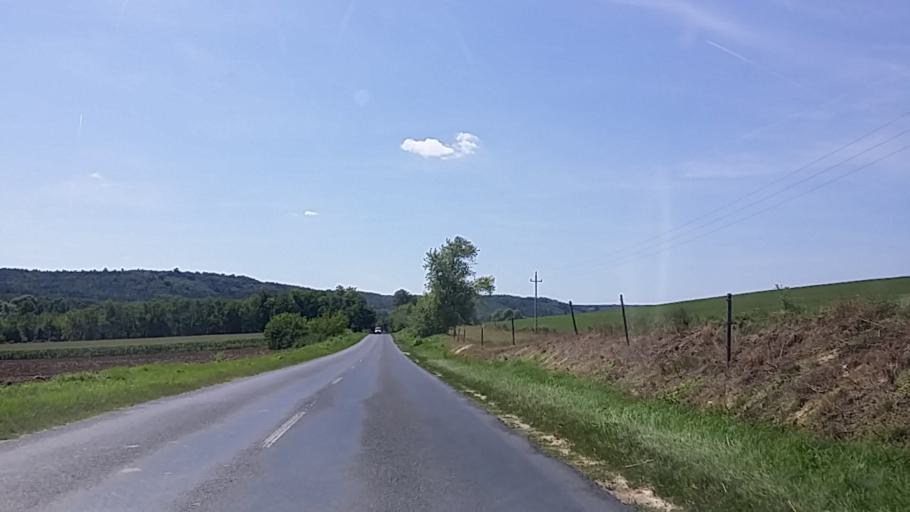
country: HU
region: Somogy
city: Tab
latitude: 46.7192
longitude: 18.0100
